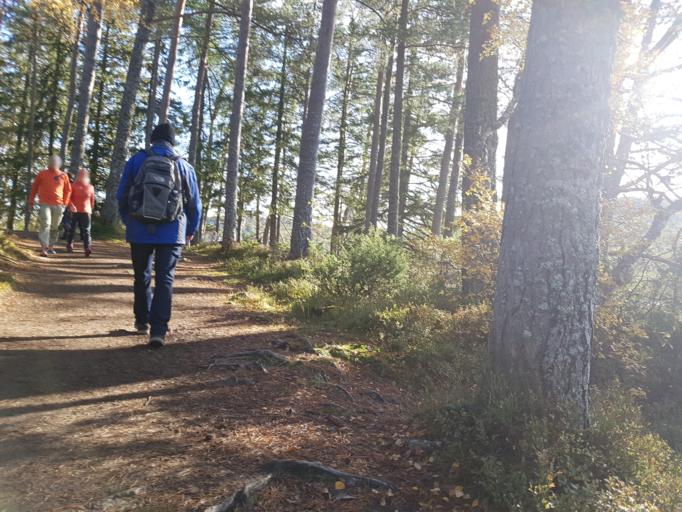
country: NO
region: Sor-Trondelag
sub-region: Trondheim
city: Trondheim
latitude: 63.4199
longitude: 10.3225
